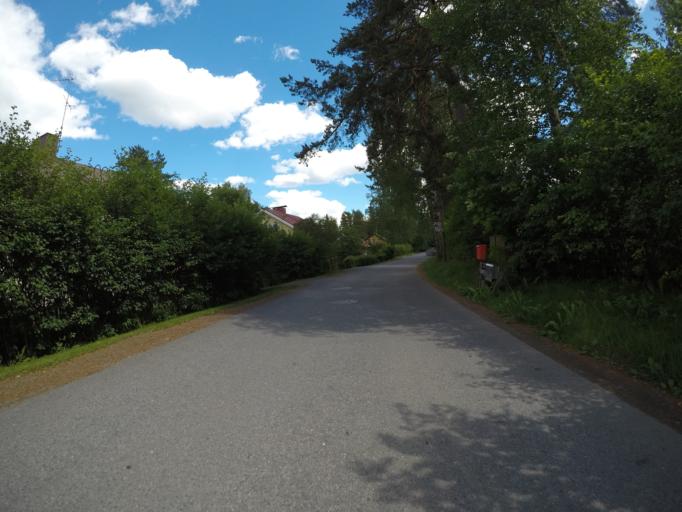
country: FI
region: Haeme
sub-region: Haemeenlinna
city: Haemeenlinna
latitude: 61.0178
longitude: 24.4306
